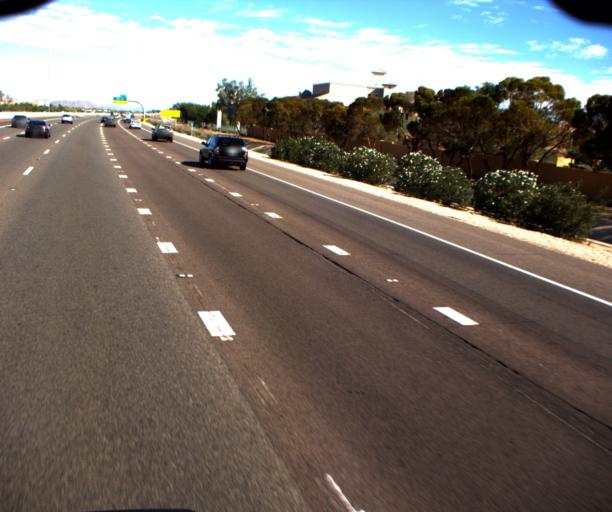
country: US
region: Arizona
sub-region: Maricopa County
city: Sun City
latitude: 33.6267
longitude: -112.2401
